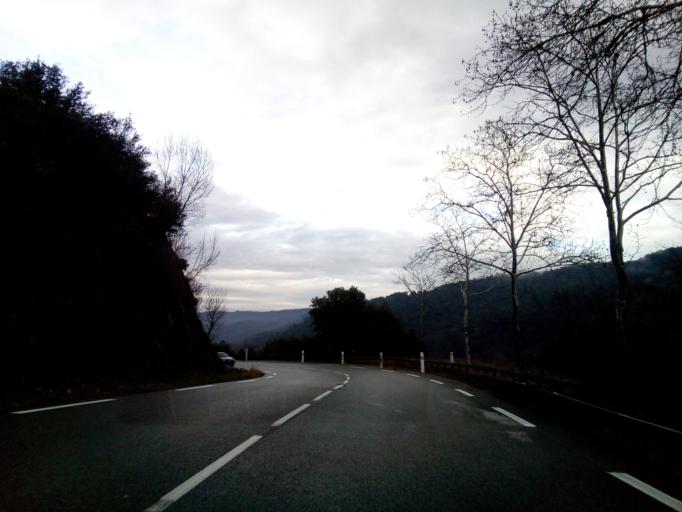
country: FR
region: Rhone-Alpes
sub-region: Departement de l'Ardeche
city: Saint-Laurent-du-Pape
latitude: 44.8202
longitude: 4.7158
